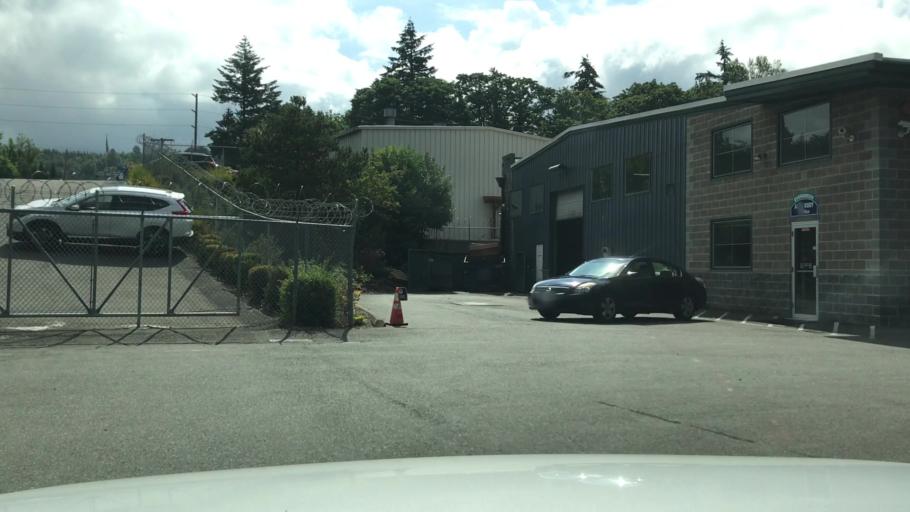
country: US
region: Washington
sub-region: King County
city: Issaquah
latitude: 47.5446
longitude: -122.0356
